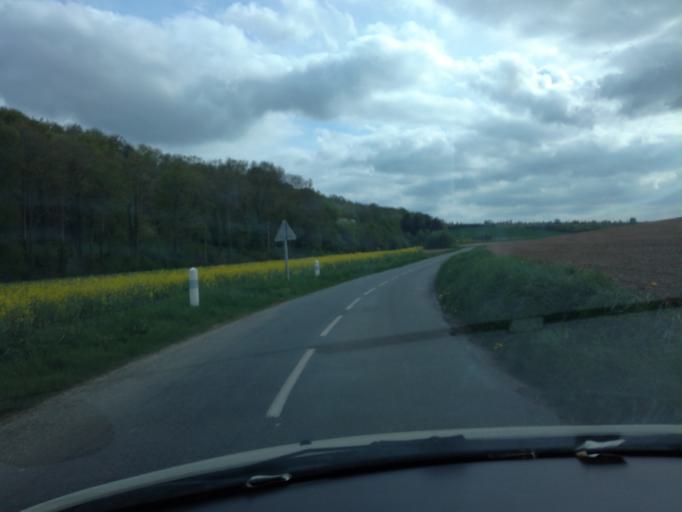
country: FR
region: Picardie
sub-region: Departement de la Somme
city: Poix-de-Picardie
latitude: 49.8171
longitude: 2.0172
